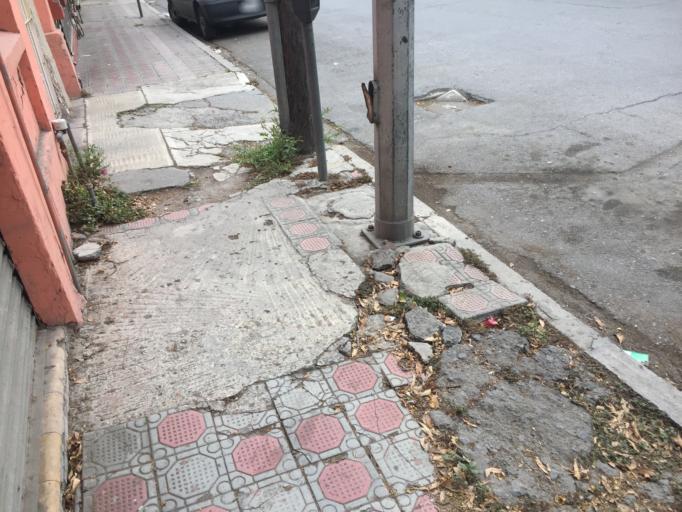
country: MX
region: Nuevo Leon
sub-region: Monterrey
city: Monterrey
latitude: 25.6808
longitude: -100.3041
